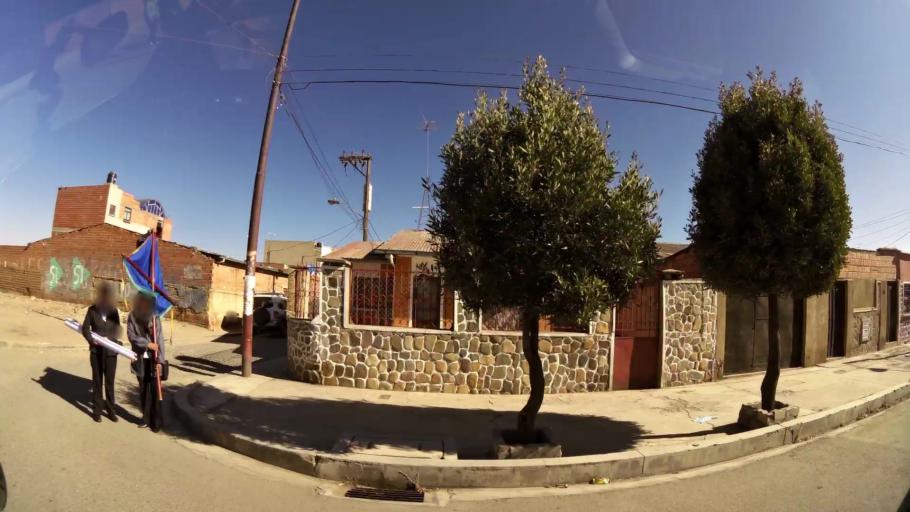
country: BO
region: La Paz
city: La Paz
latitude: -16.5239
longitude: -68.2070
